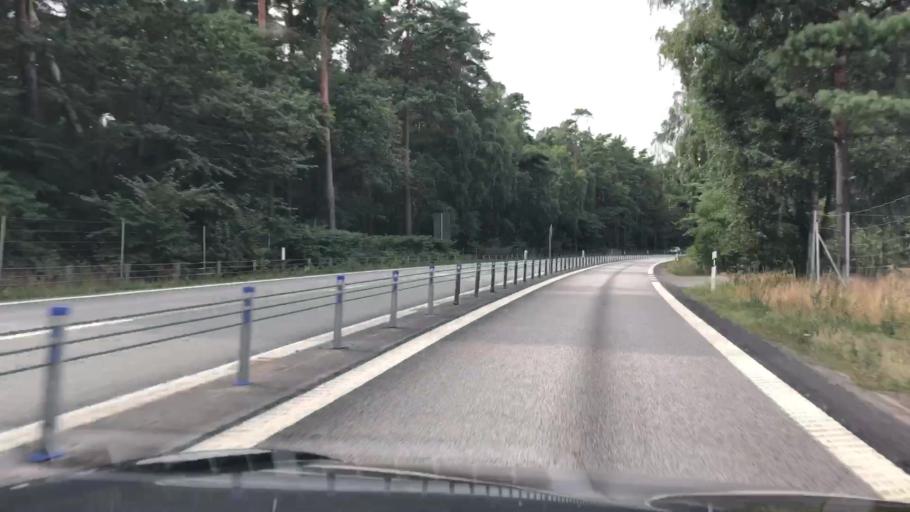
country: SE
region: Skane
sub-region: Kristianstads Kommun
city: Fjalkinge
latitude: 56.0365
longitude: 14.3792
